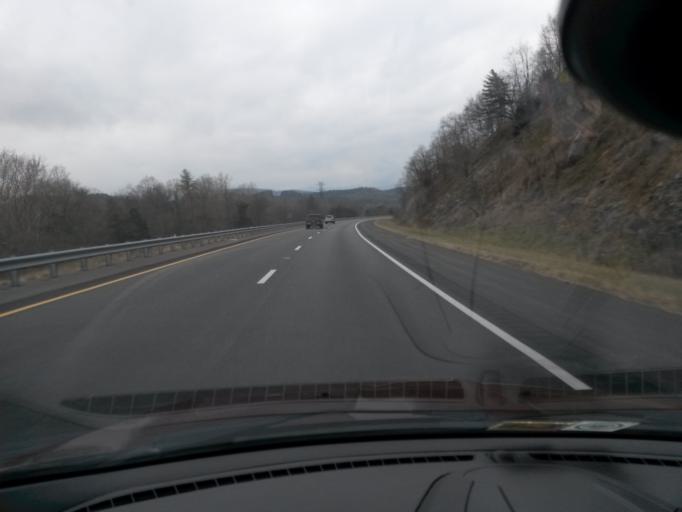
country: US
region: Virginia
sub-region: Alleghany County
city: Clifton Forge
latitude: 37.7973
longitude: -79.7283
